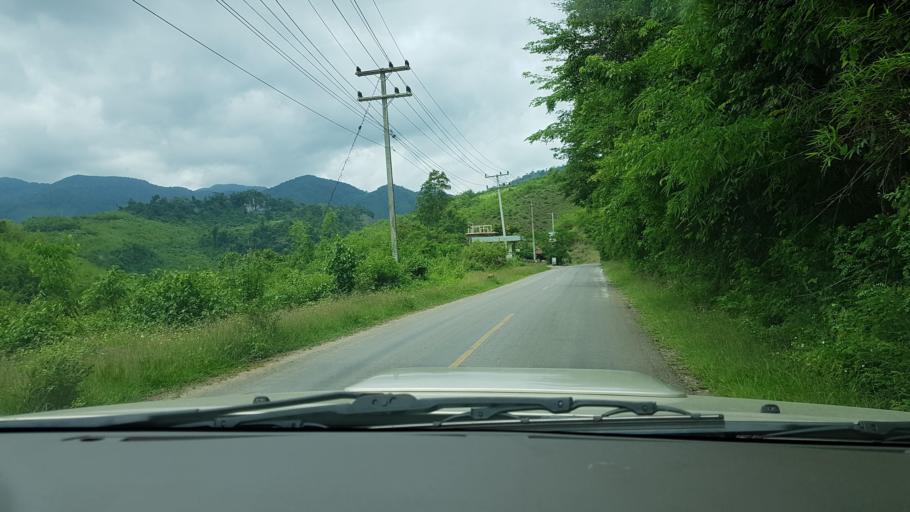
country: TH
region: Nan
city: Chaloem Phra Kiat
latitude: 19.9542
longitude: 101.2552
